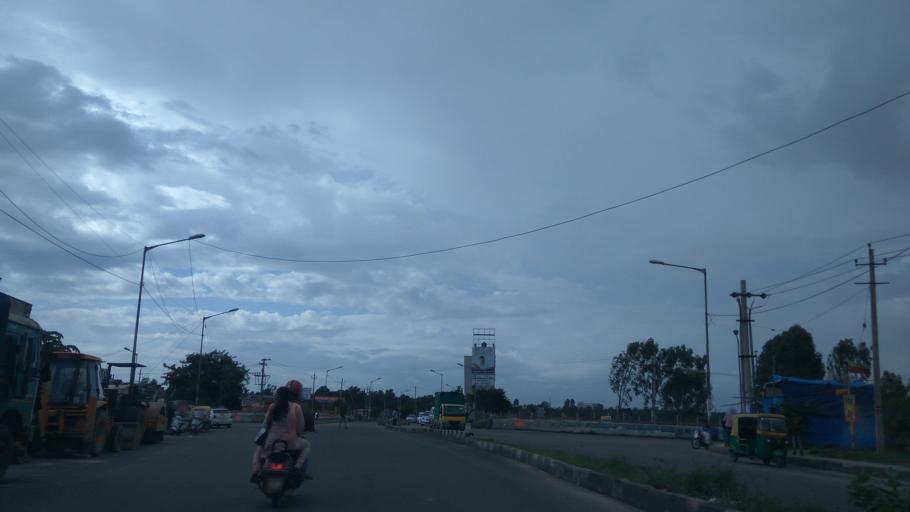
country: IN
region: Karnataka
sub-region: Bangalore Urban
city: Yelahanka
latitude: 13.1010
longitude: 77.6351
